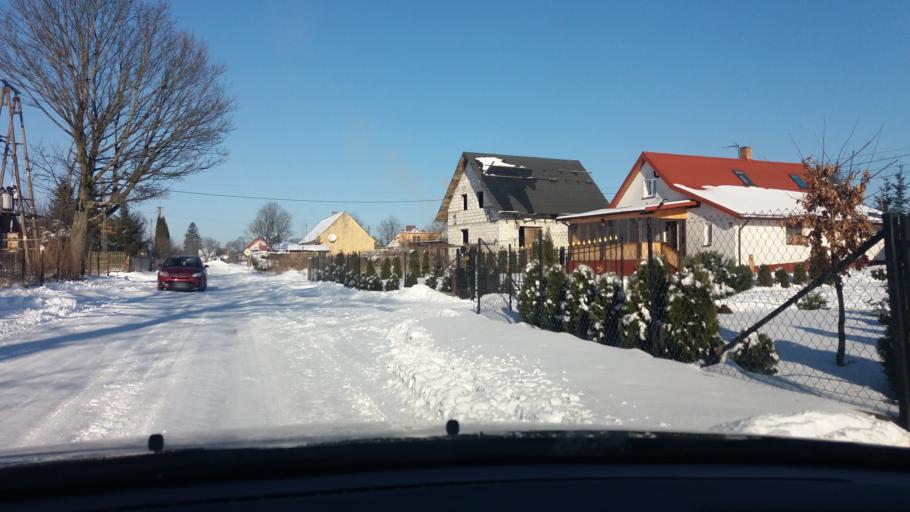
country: PL
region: Warmian-Masurian Voivodeship
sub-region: Powiat nidzicki
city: Nidzica
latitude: 53.3764
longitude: 20.6079
